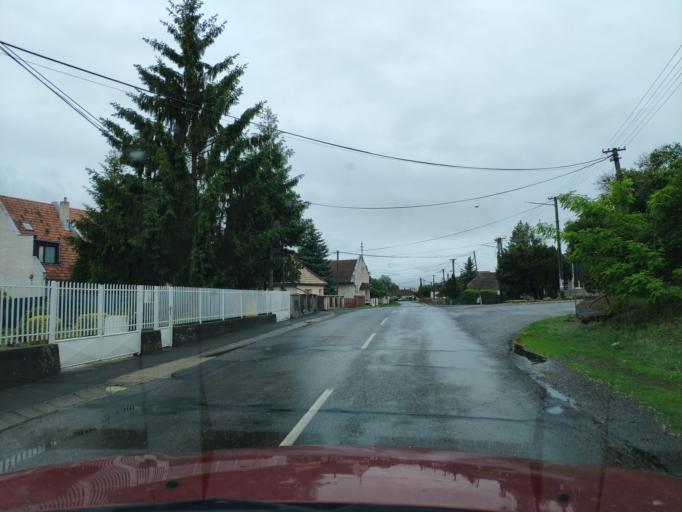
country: SK
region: Kosicky
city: Cierna nad Tisou
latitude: 48.4126
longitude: 22.0585
